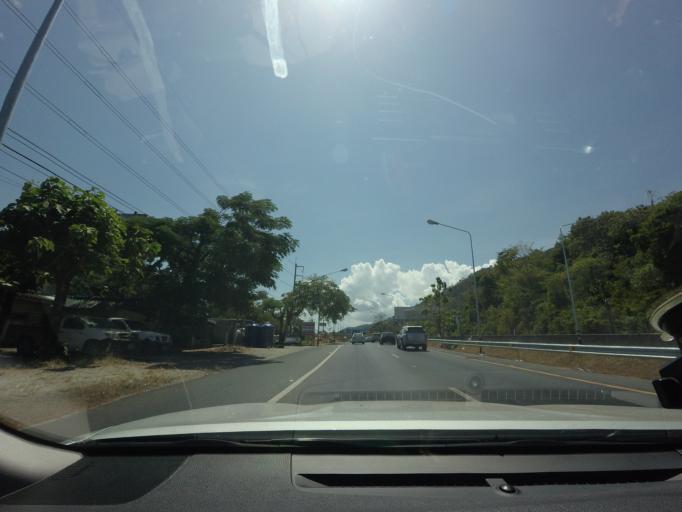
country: TH
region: Phuket
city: Ban Ko Kaeo
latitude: 7.9434
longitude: 98.3822
